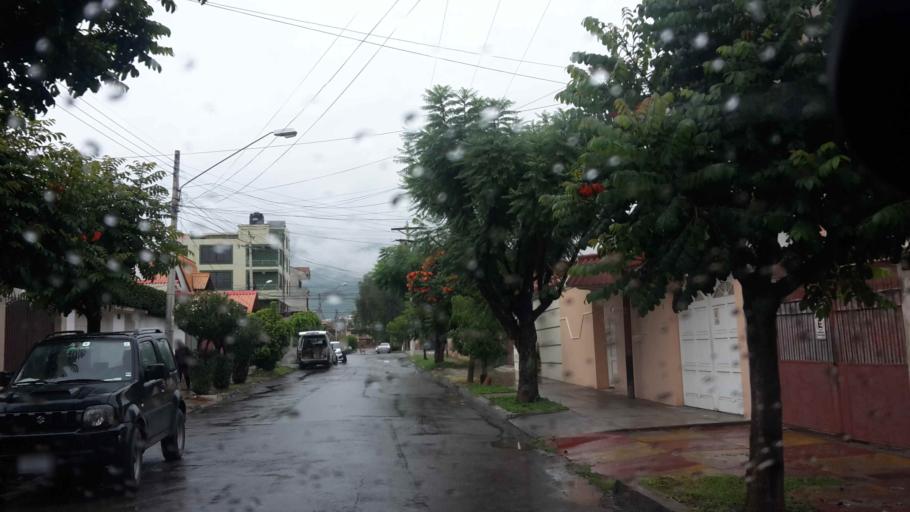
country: BO
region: Cochabamba
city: Cochabamba
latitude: -17.3769
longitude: -66.1643
